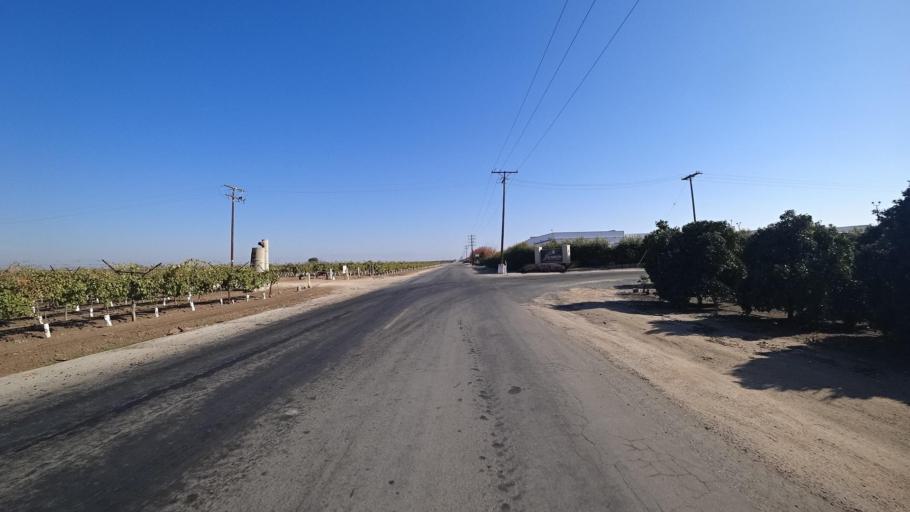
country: US
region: California
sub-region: Kern County
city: McFarland
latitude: 35.7180
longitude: -119.1521
